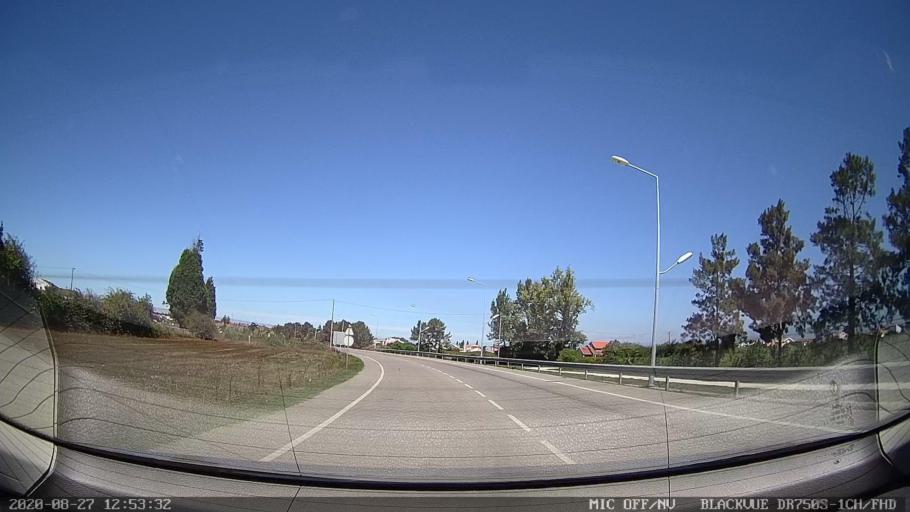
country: PT
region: Aveiro
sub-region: Ilhavo
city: Ilhavo
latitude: 40.5998
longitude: -8.6778
